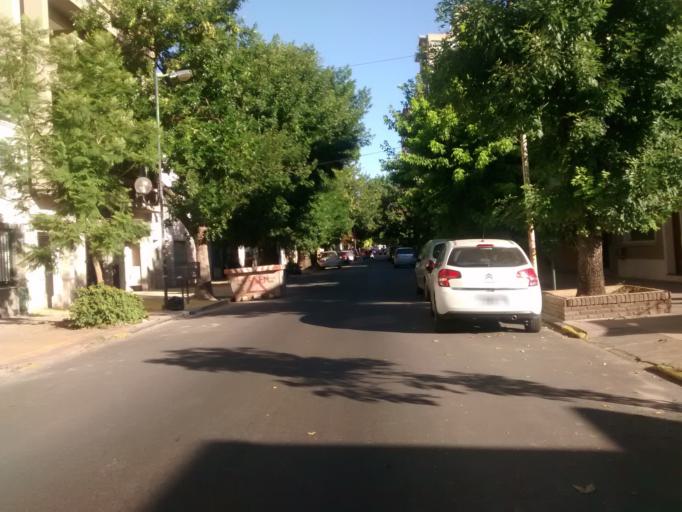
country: AR
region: Buenos Aires
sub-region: Partido de La Plata
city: La Plata
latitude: -34.9287
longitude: -57.9517
